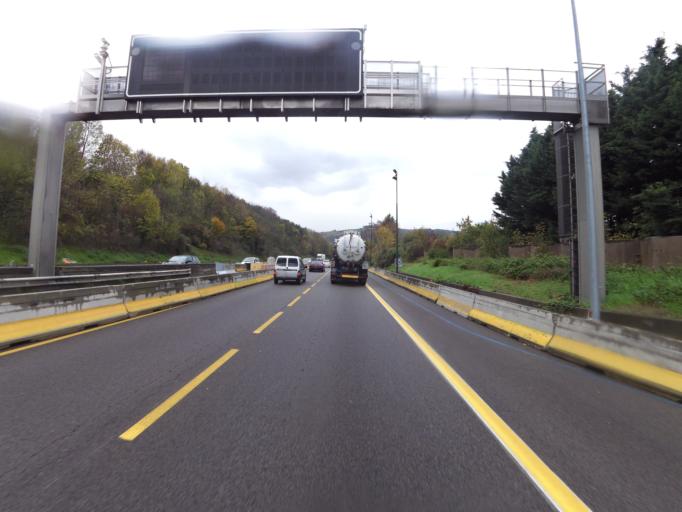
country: FR
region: Rhone-Alpes
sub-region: Departement du Rhone
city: Saint-Romain-en-Gal
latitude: 45.5330
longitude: 4.8597
